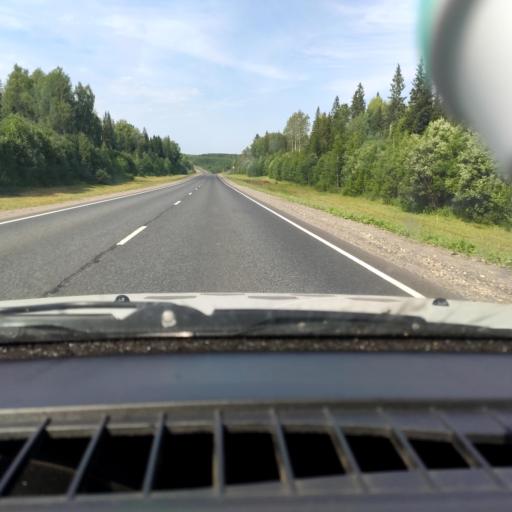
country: RU
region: Kirov
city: Kostino
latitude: 58.7630
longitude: 53.6098
